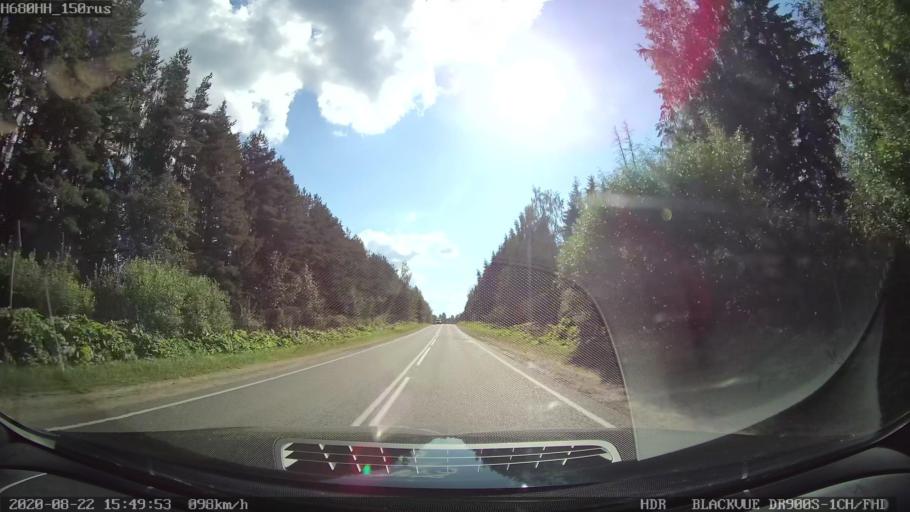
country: RU
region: Tverskaya
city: Bezhetsk
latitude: 57.6747
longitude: 36.4514
